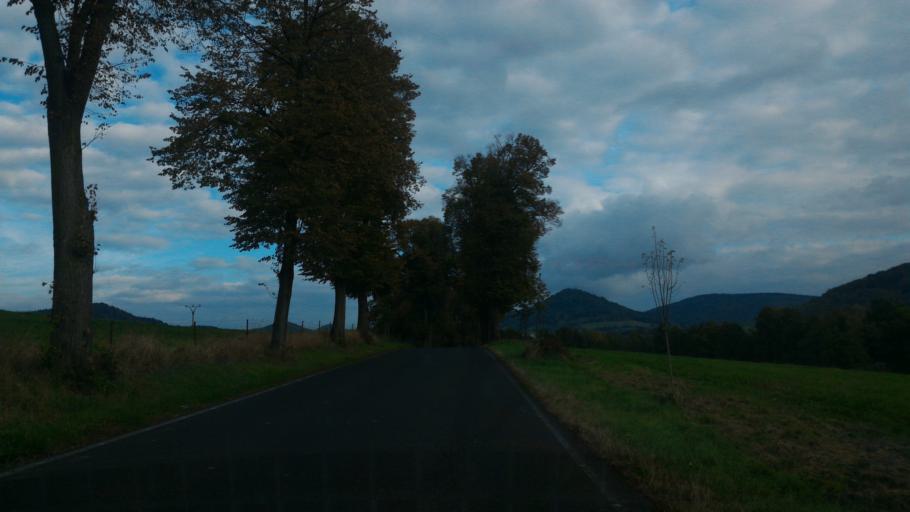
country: CZ
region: Ustecky
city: Ceska Kamenice
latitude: 50.8029
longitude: 14.3924
